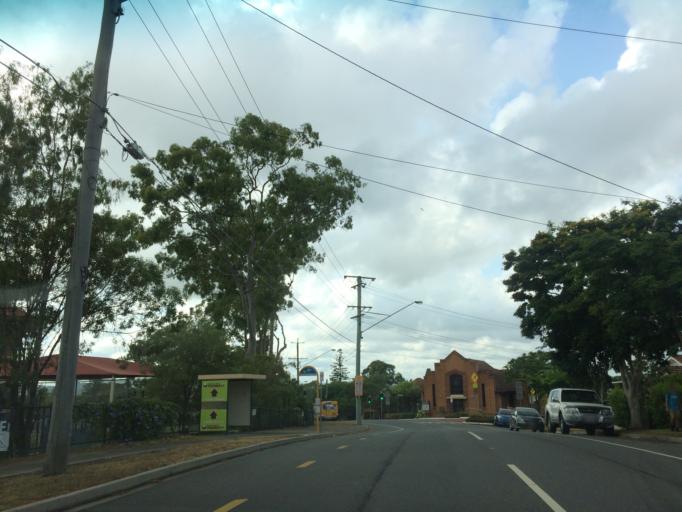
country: AU
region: Queensland
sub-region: Brisbane
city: Toowong
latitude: -27.5001
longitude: 152.9954
